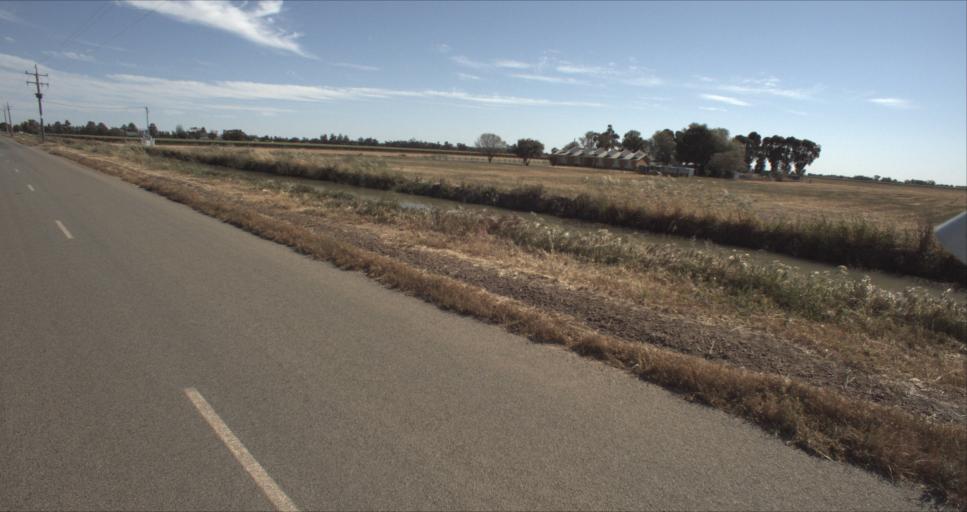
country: AU
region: New South Wales
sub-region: Leeton
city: Leeton
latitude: -34.5765
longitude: 146.3807
